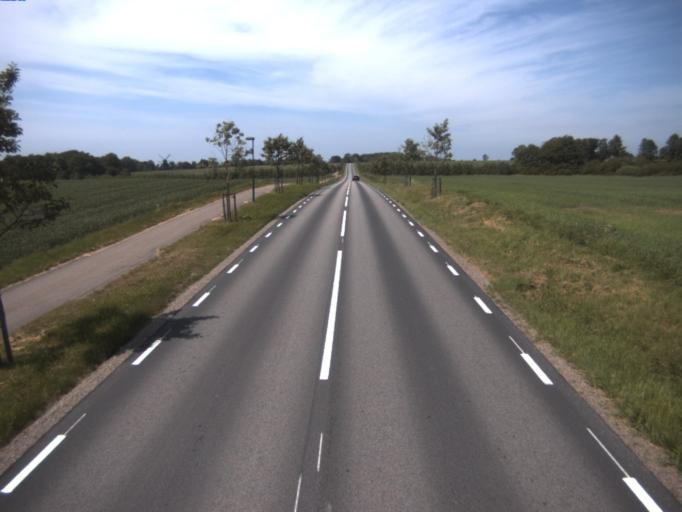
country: SE
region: Skane
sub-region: Helsingborg
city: Helsingborg
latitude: 56.0993
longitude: 12.6499
